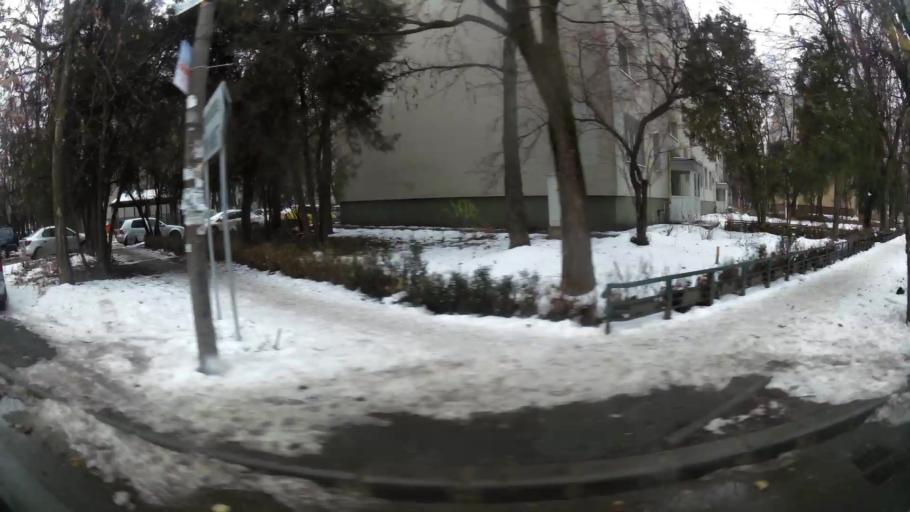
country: RO
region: Ilfov
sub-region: Comuna Chiajna
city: Rosu
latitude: 44.4375
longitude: 26.0420
